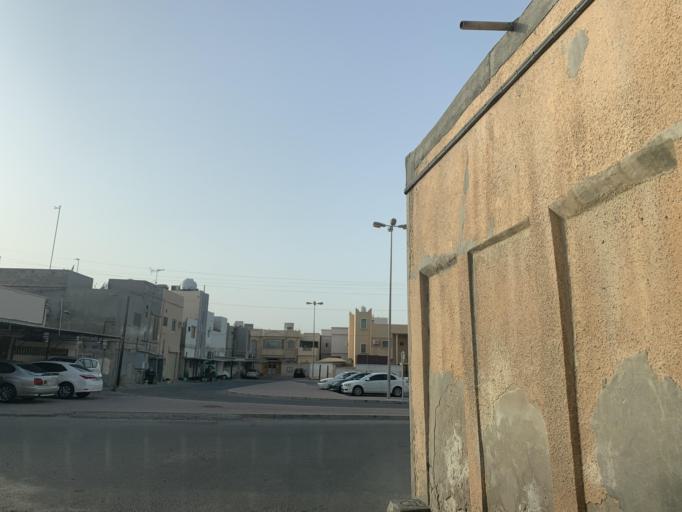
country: BH
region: Northern
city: Madinat `Isa
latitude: 26.1590
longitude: 50.5156
